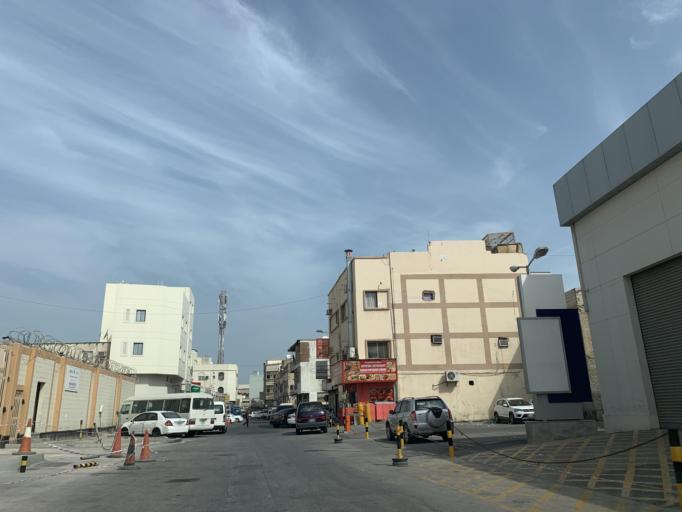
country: BH
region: Manama
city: Manama
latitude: 26.2255
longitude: 50.5750
